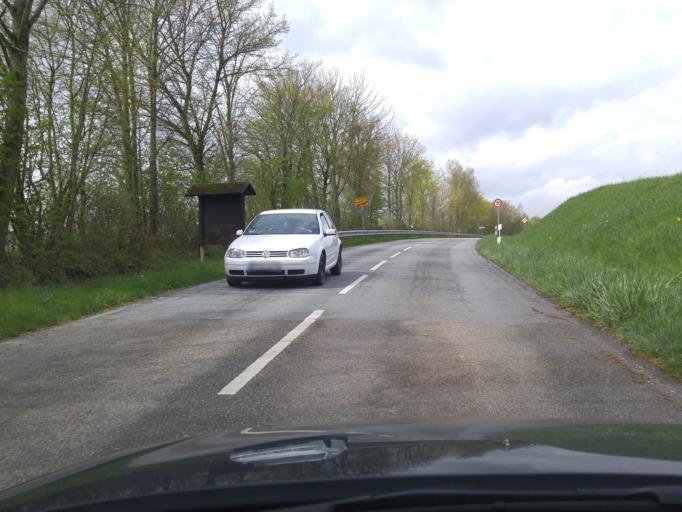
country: DE
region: Baden-Wuerttemberg
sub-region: Karlsruhe Region
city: Spechbach
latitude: 49.3492
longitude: 8.8816
